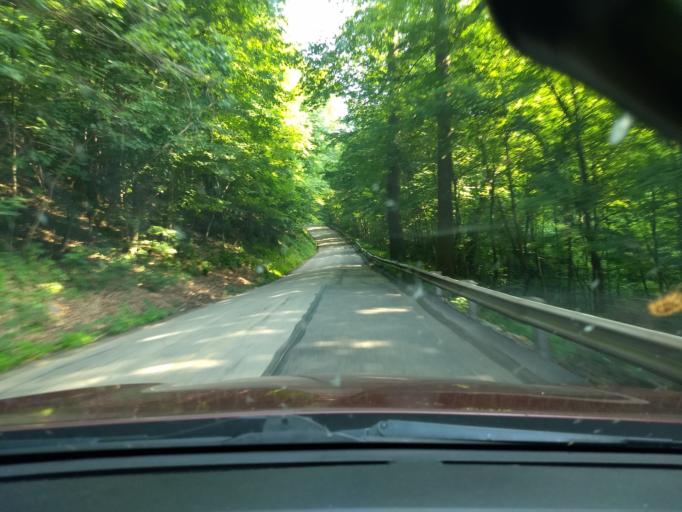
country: US
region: Pennsylvania
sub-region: Westmoreland County
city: Trafford
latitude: 40.3676
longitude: -79.7639
